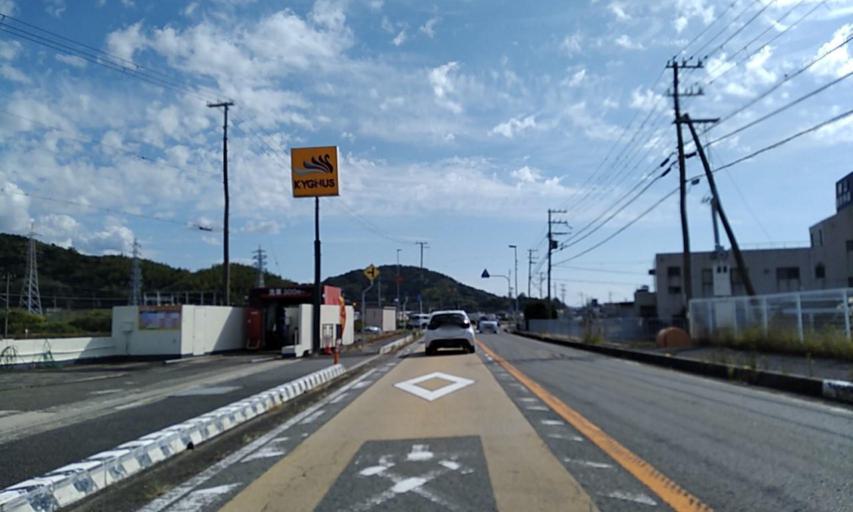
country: JP
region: Wakayama
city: Gobo
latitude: 33.9221
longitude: 135.1454
